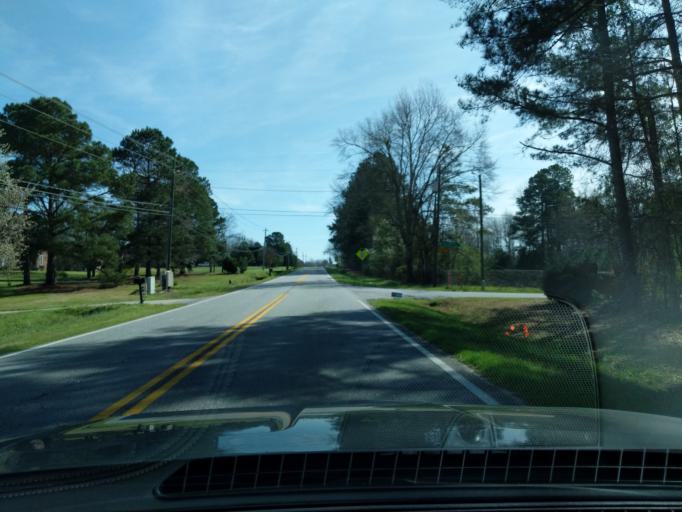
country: US
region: Georgia
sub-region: Columbia County
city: Evans
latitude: 33.5303
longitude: -82.1643
